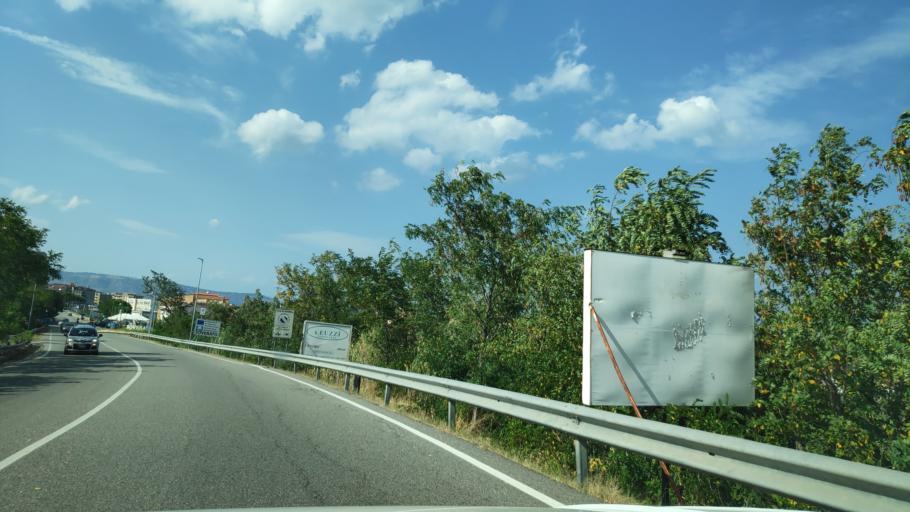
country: IT
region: Calabria
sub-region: Provincia di Catanzaro
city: Soverato Marina
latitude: 38.6782
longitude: 16.5514
